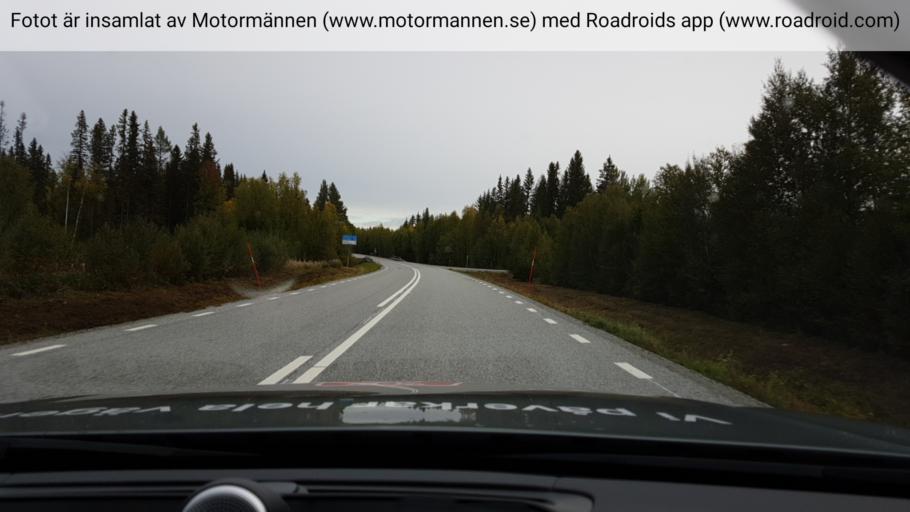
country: SE
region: Jaemtland
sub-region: Stroemsunds Kommun
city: Stroemsund
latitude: 64.1416
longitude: 15.6813
